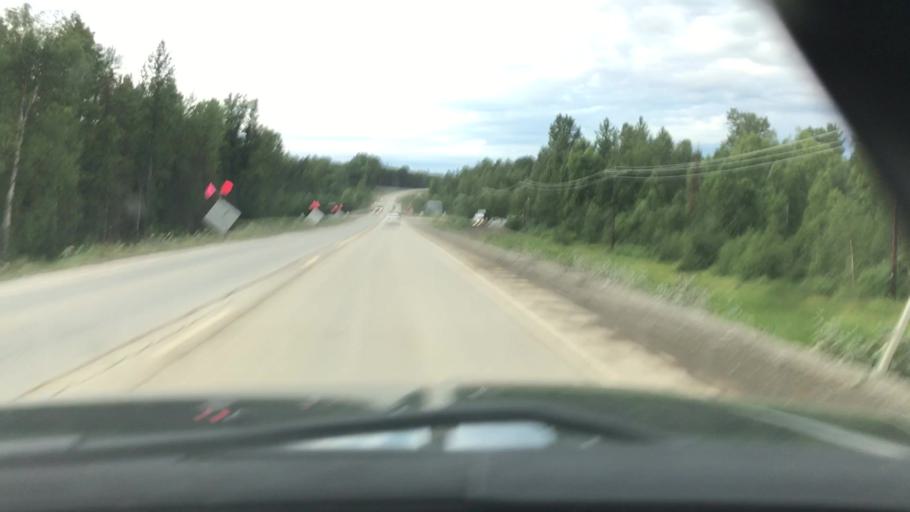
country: US
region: Alaska
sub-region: Matanuska-Susitna Borough
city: Y
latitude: 62.1014
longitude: -150.0606
